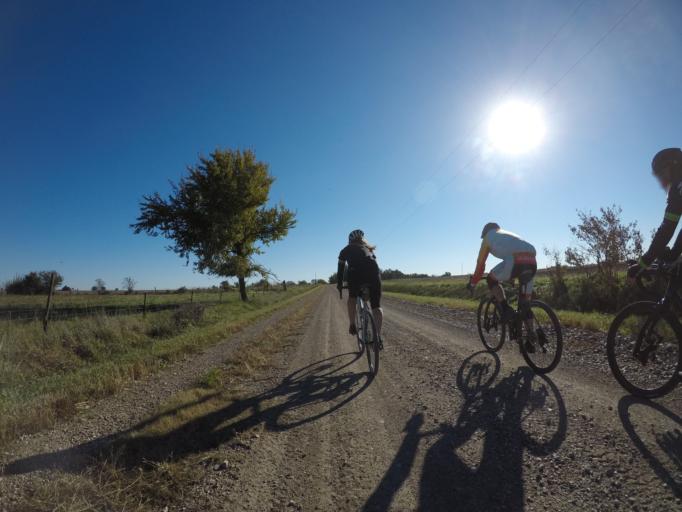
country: US
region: Kansas
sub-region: Morris County
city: Council Grove
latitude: 38.8258
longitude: -96.4414
